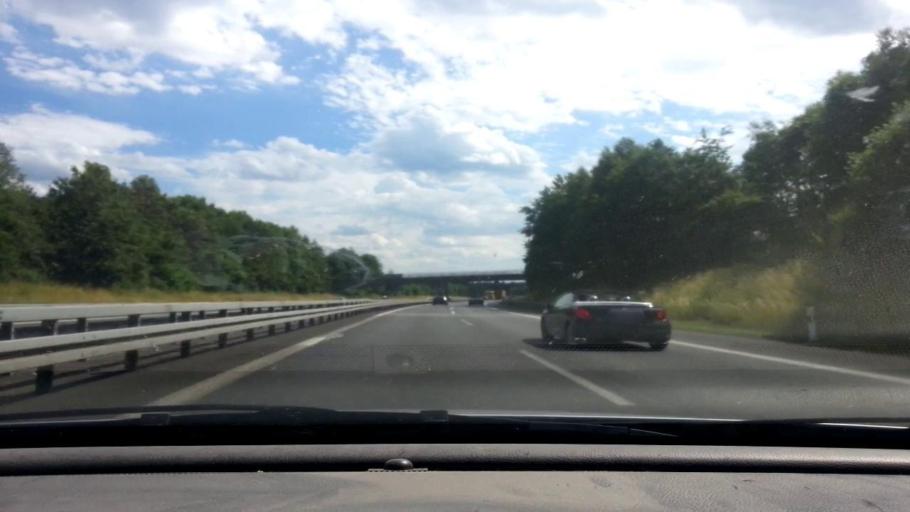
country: DE
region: Bavaria
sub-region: Upper Palatinate
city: Mitterteich
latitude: 49.9285
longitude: 12.2268
